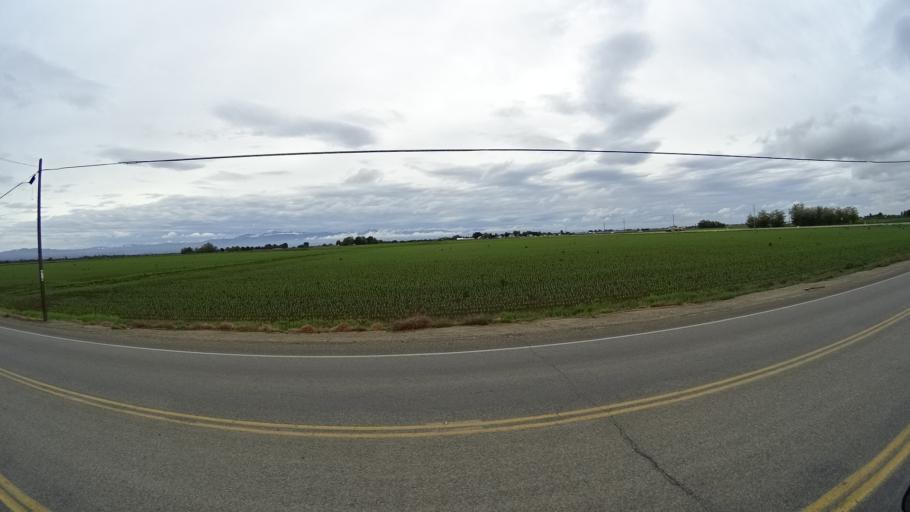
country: US
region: Idaho
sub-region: Ada County
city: Star
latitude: 43.6645
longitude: -116.4935
